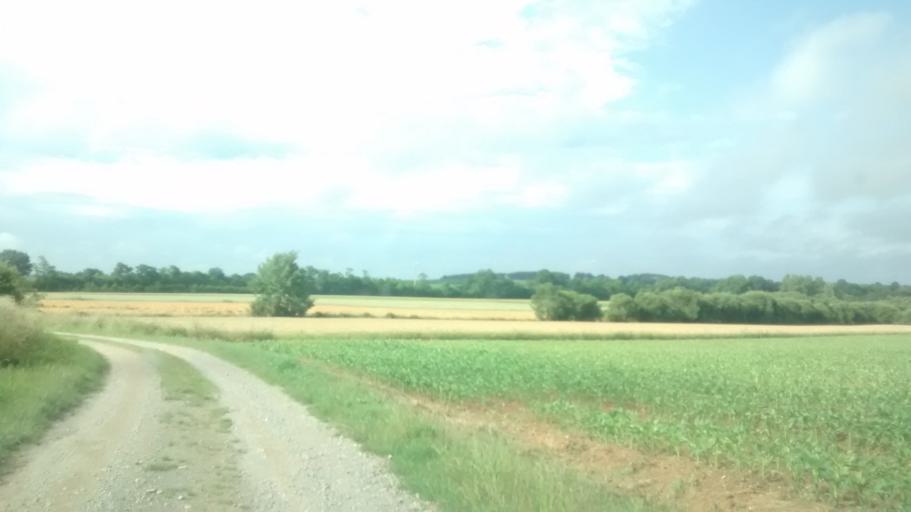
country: FR
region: Brittany
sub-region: Departement d'Ille-et-Vilaine
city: Plechatel
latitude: 47.8385
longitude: -1.7468
